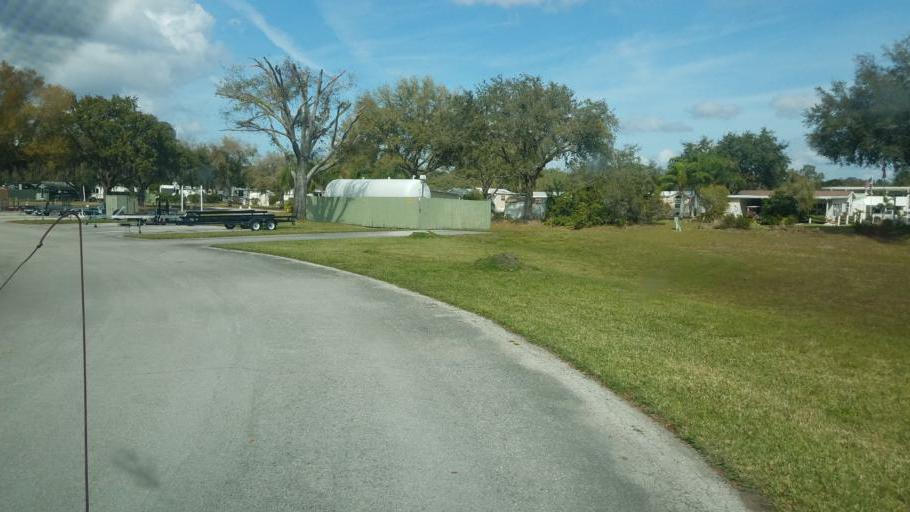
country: US
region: Florida
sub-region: Osceola County
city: Poinciana
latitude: 27.9743
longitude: -81.3779
